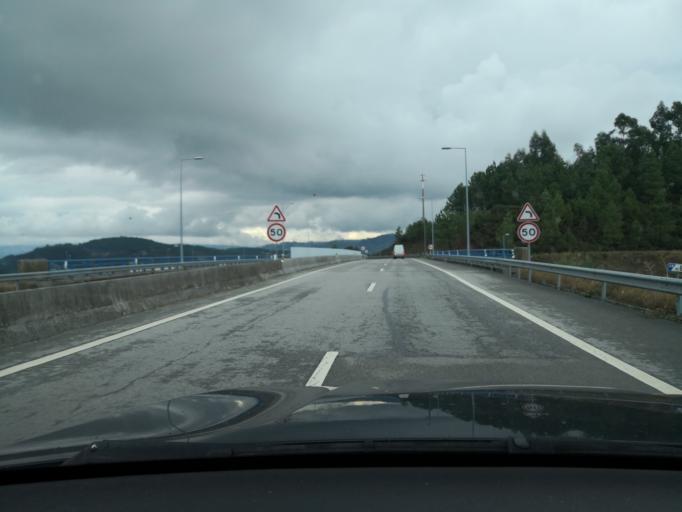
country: PT
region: Porto
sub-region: Lousada
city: Lousada
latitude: 41.2927
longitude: -8.2653
